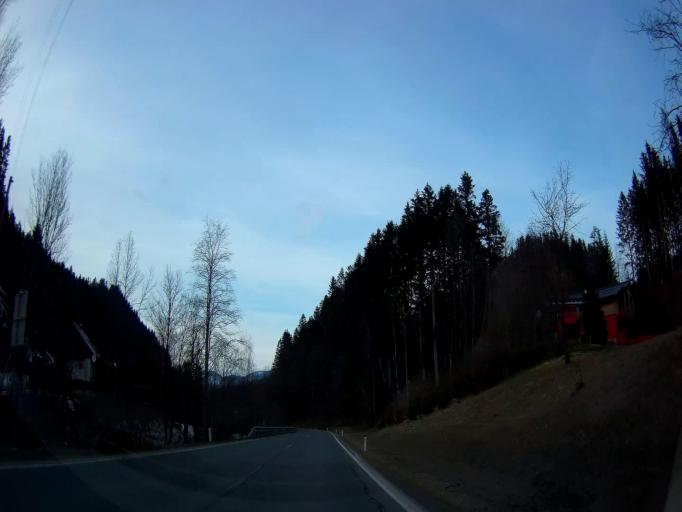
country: AT
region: Salzburg
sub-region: Politischer Bezirk Hallein
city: Abtenau
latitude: 47.5340
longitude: 13.4239
